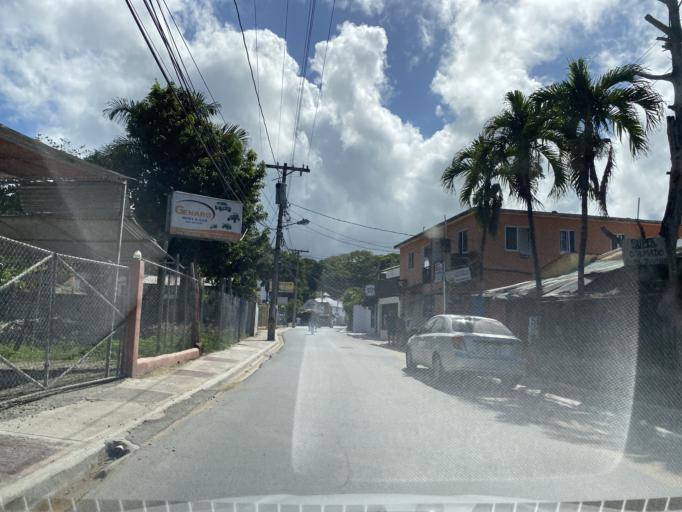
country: DO
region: Samana
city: Las Terrenas
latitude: 19.3182
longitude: -69.5409
